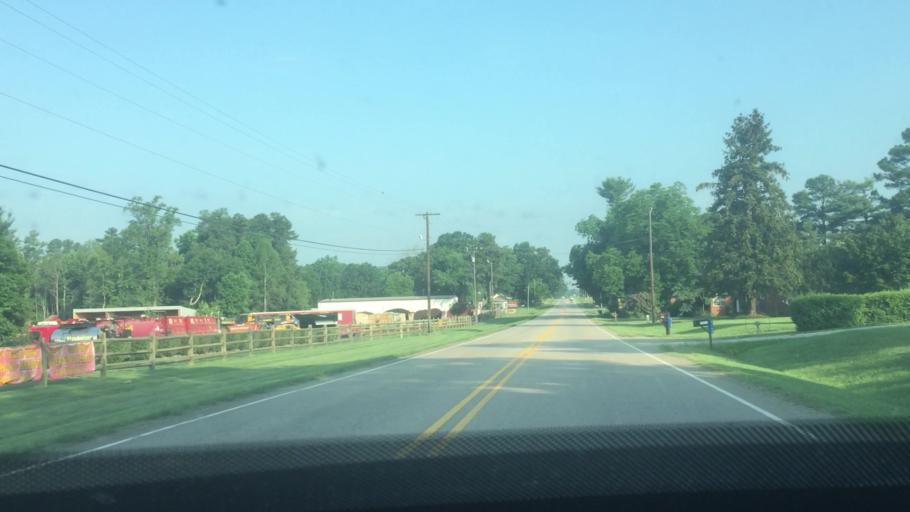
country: US
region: North Carolina
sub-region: Iredell County
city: Mooresville
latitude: 35.5830
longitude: -80.7386
